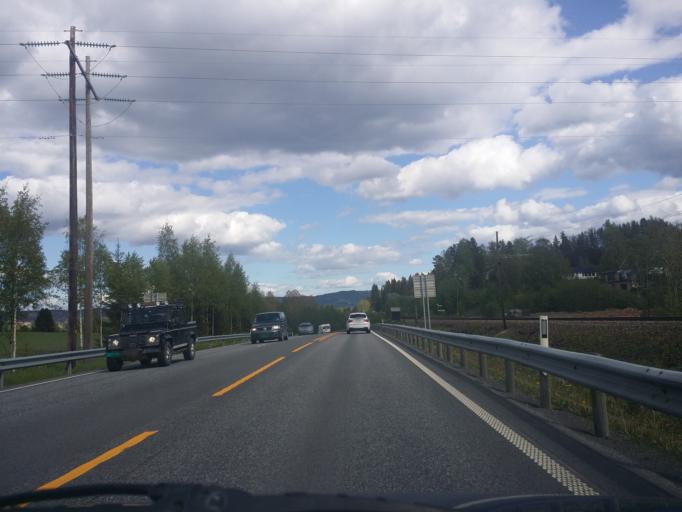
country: NO
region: Oppland
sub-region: Lunner
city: Roa
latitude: 60.2937
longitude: 10.5741
